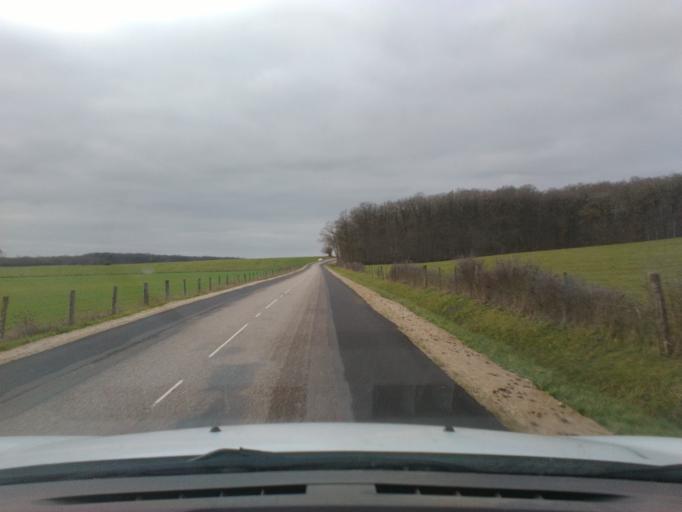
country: FR
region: Lorraine
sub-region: Departement des Vosges
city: Mirecourt
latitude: 48.3373
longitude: 6.0046
